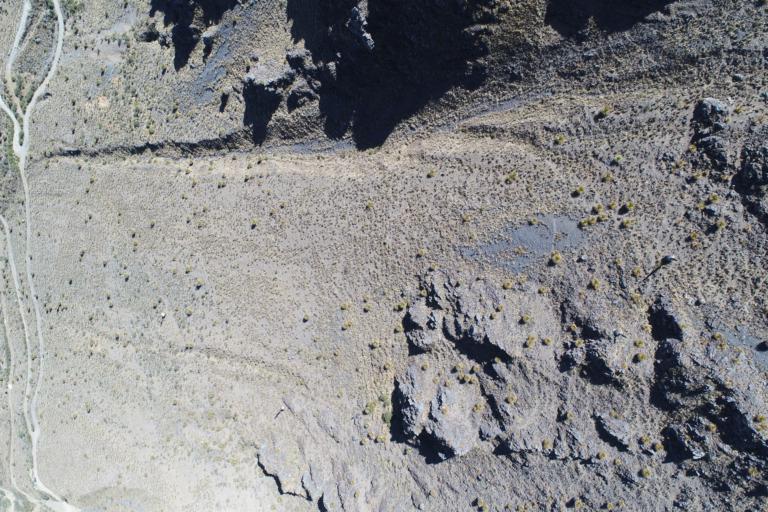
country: BO
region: La Paz
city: Viloco
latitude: -16.8067
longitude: -67.5487
